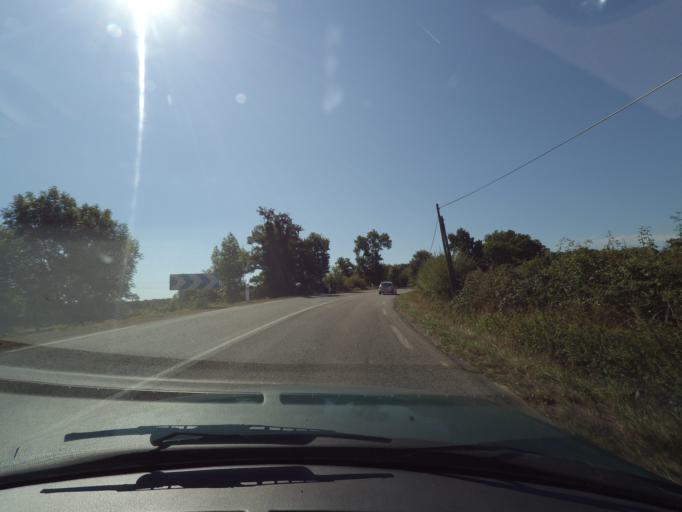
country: FR
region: Limousin
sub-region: Departement de la Haute-Vienne
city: Bellac
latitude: 46.0956
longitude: 1.0806
